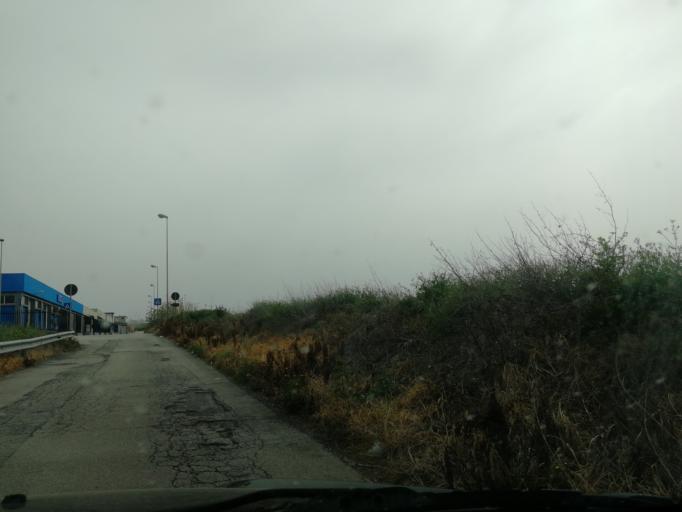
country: IT
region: Apulia
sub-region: Provincia di Barletta - Andria - Trani
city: Barletta
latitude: 41.3155
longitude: 16.3115
